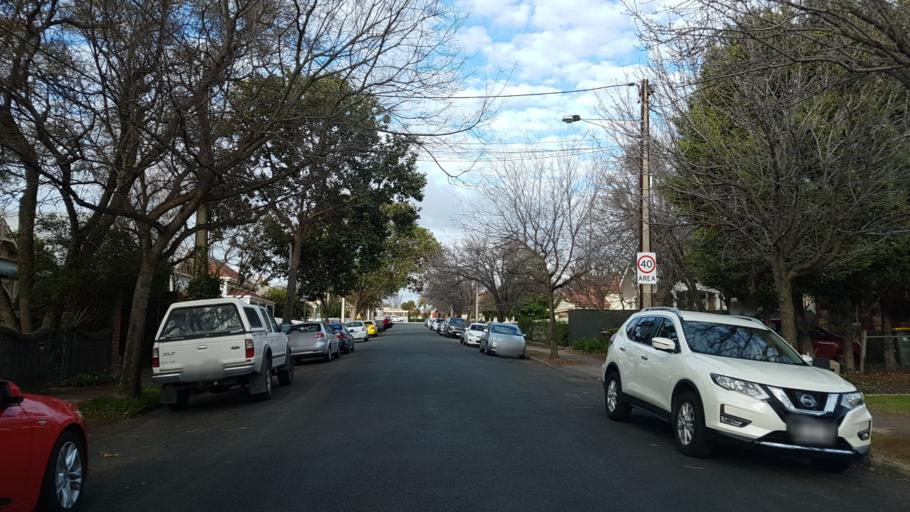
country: AU
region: South Australia
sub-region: Prospect
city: Prospect
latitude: -34.8893
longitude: 138.5922
